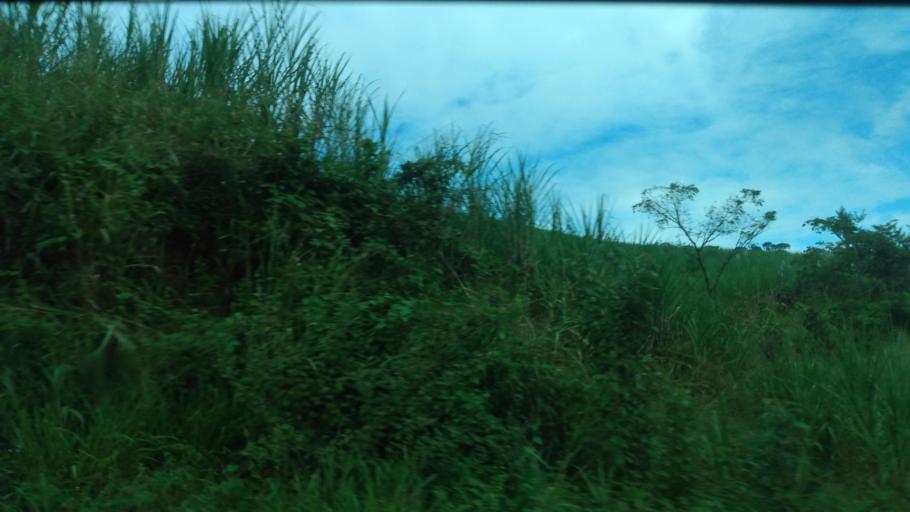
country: BR
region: Pernambuco
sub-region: Maraial
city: Maraial
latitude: -8.7162
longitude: -35.7777
